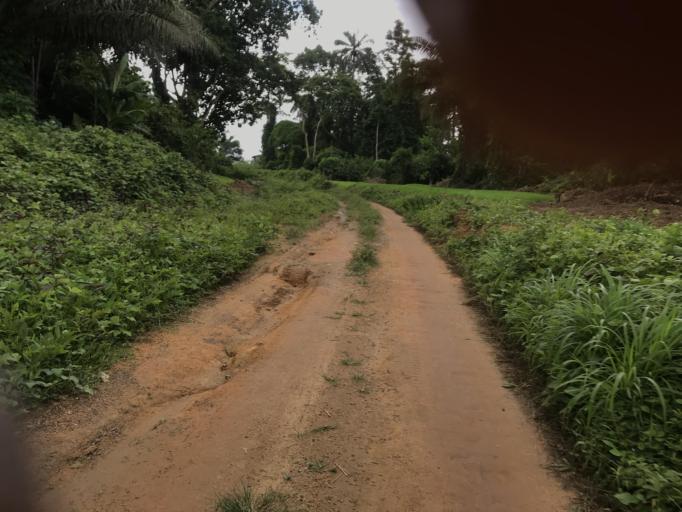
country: GN
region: Nzerekore
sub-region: Prefecture de Guekedou
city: Gueckedou
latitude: 8.4728
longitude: -10.2845
